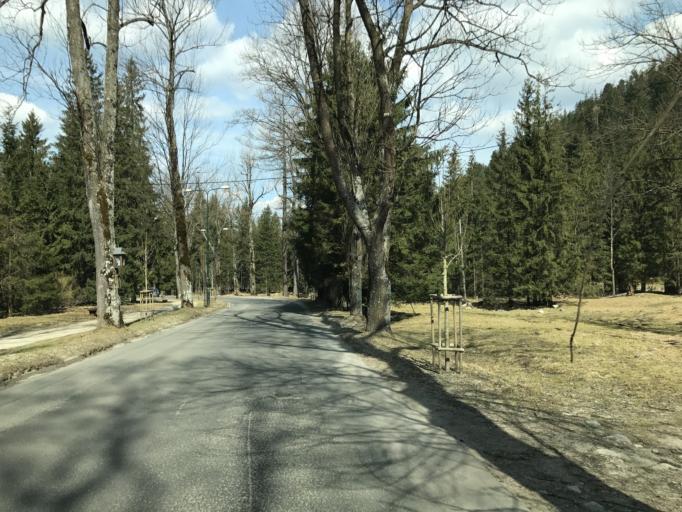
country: PL
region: Lesser Poland Voivodeship
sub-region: Powiat tatrzanski
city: Zakopane
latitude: 49.2771
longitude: 19.9809
